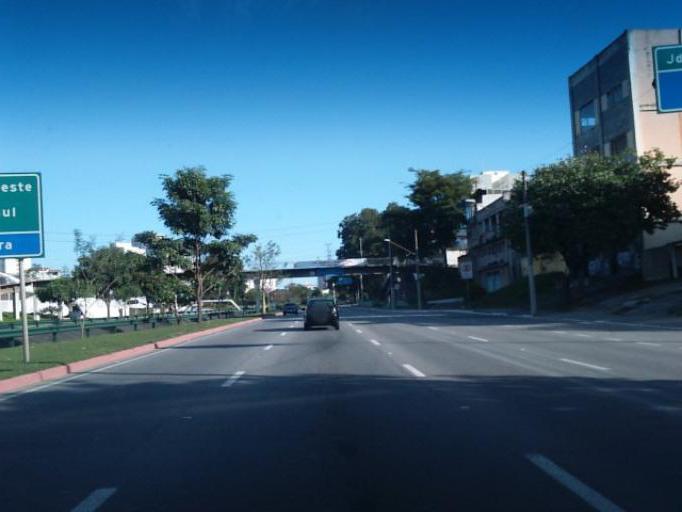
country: BR
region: Sao Paulo
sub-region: Sao Jose Dos Campos
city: Sao Jose dos Campos
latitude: -23.1940
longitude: -45.8841
